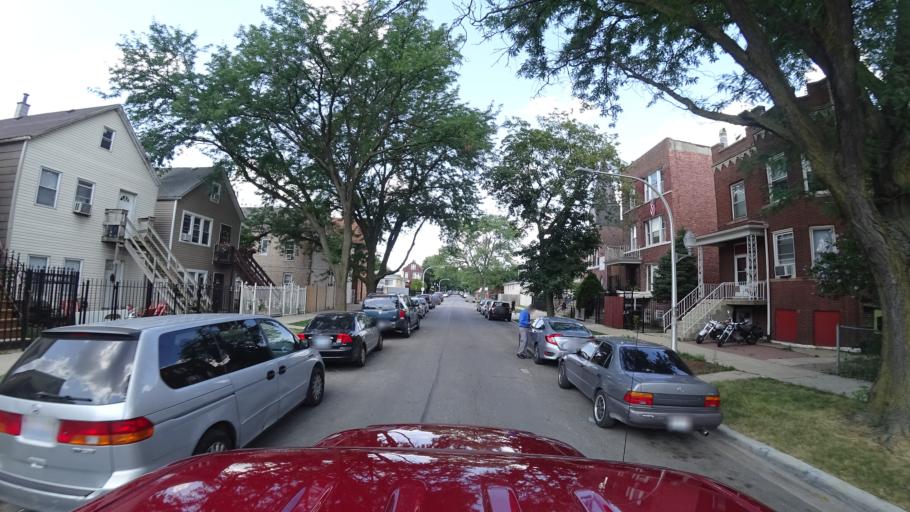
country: US
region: Illinois
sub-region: Cook County
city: Chicago
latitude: 41.8236
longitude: -87.7007
